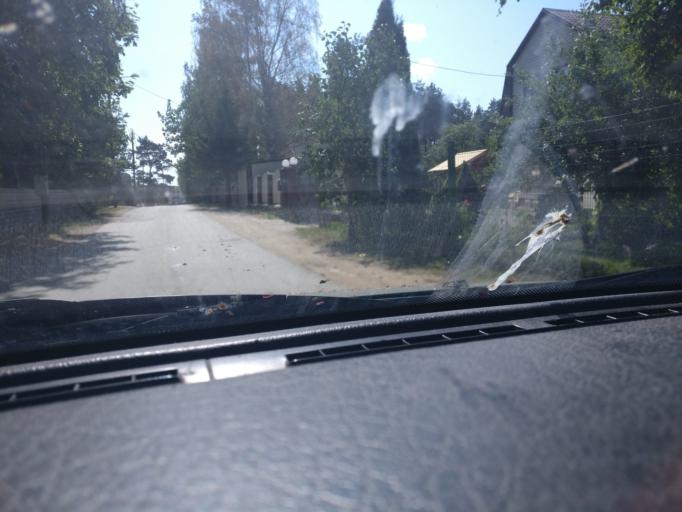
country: EE
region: Tartu
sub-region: Tartu linn
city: Tartu
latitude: 58.3496
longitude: 26.7894
